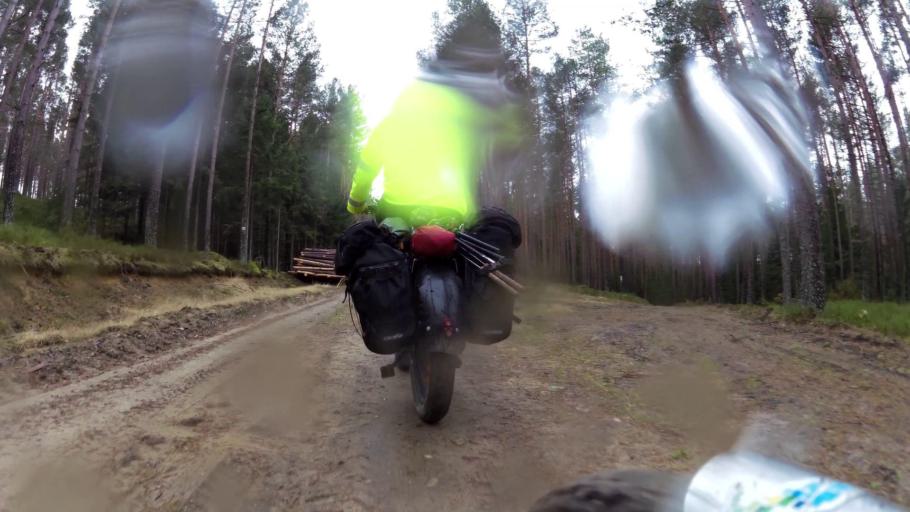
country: PL
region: Pomeranian Voivodeship
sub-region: Powiat bytowski
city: Trzebielino
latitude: 54.0773
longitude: 17.0959
